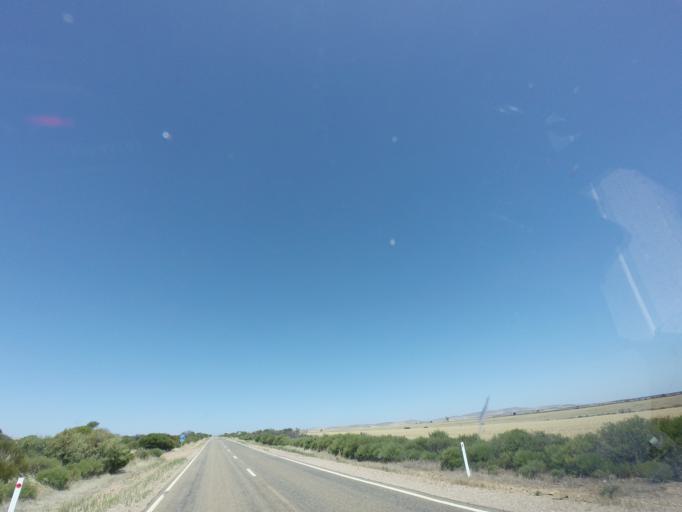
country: AU
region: South Australia
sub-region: Flinders Ranges
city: Quorn
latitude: -32.7034
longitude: 138.4047
